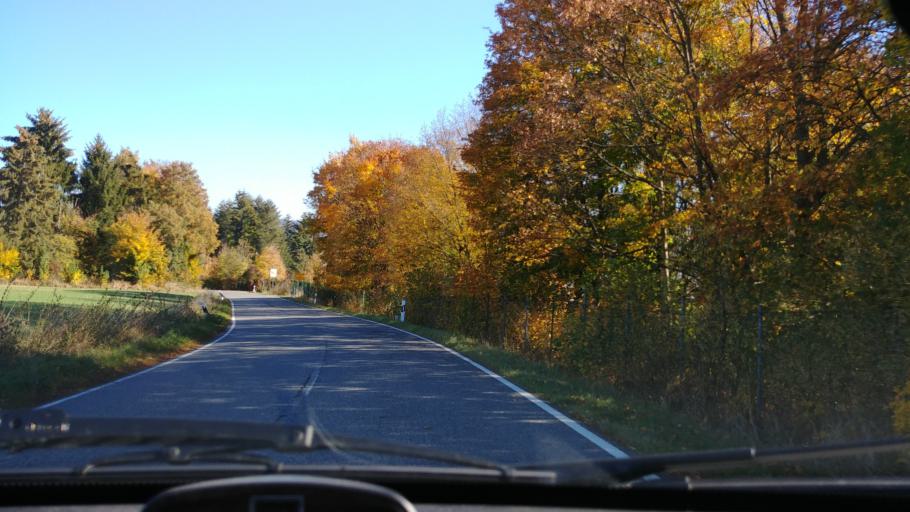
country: DE
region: Hesse
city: Taunusstein
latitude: 50.1434
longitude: 8.1386
